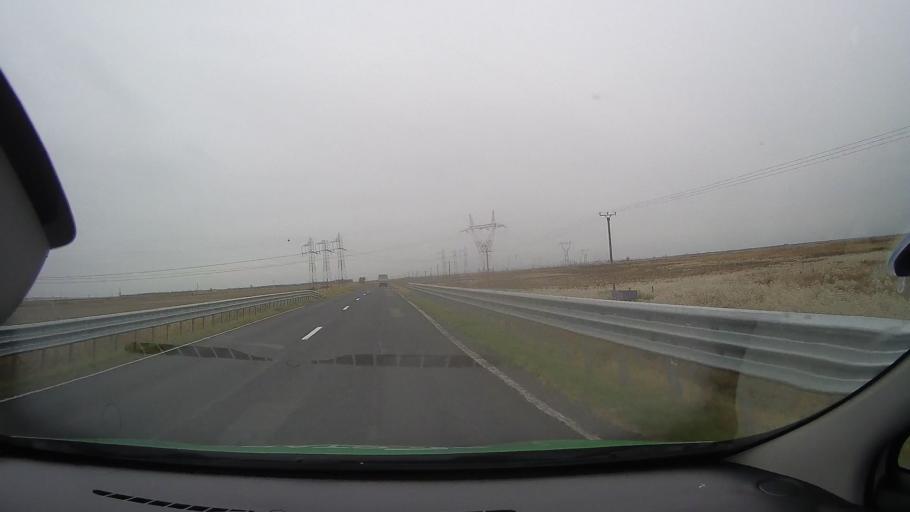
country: RO
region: Ialomita
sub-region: Comuna Gura Ialomitei
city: Gura Ialomitei
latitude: 44.6899
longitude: 27.8032
